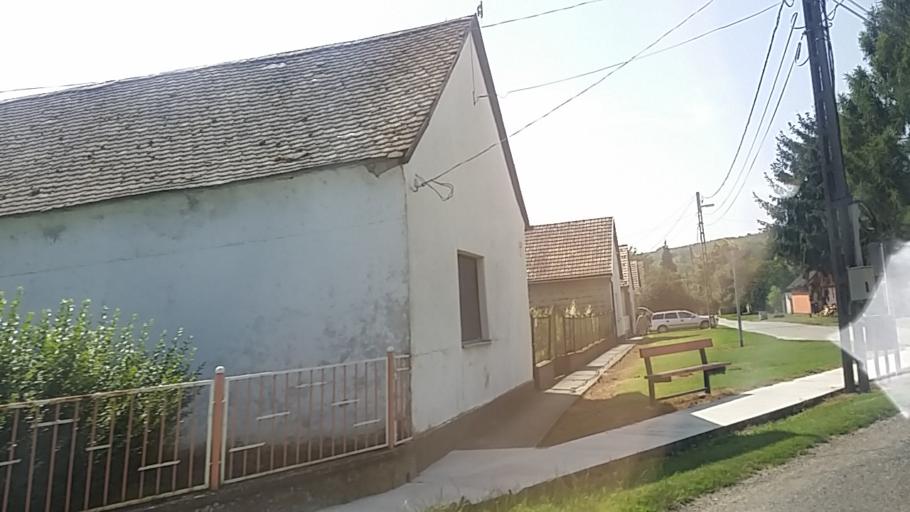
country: HU
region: Baranya
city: Siklos
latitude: 45.9040
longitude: 18.3327
